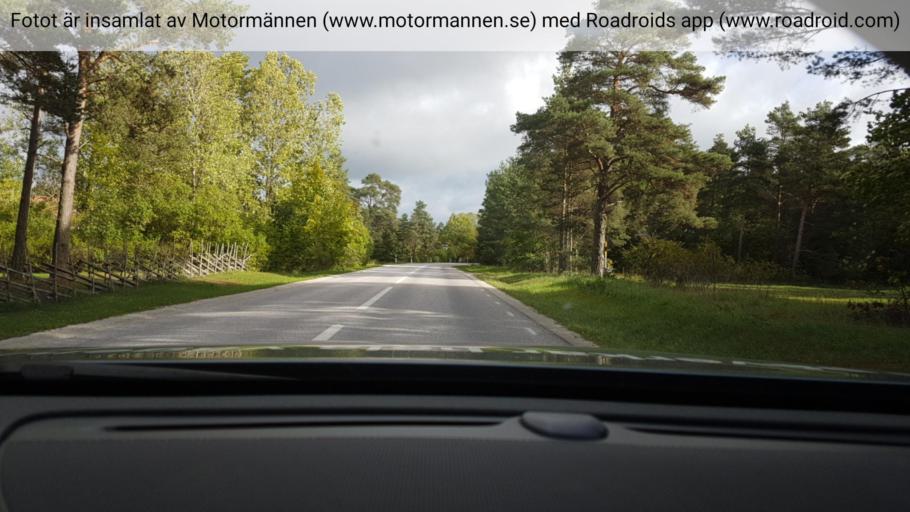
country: SE
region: Gotland
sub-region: Gotland
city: Visby
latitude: 57.6735
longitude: 18.4842
